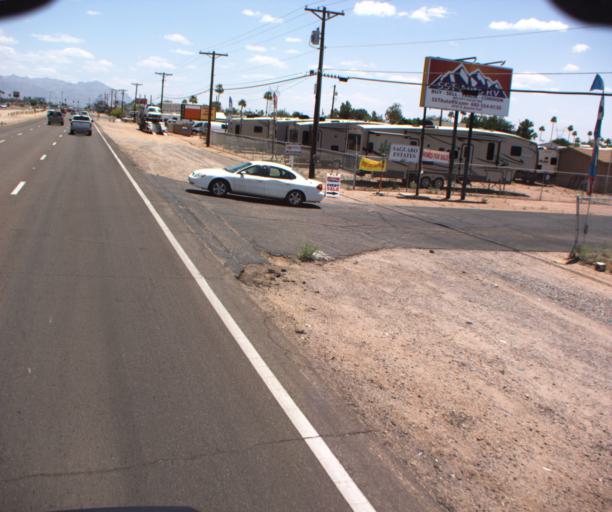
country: US
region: Arizona
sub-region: Pinal County
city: Apache Junction
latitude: 33.4151
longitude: -111.6199
